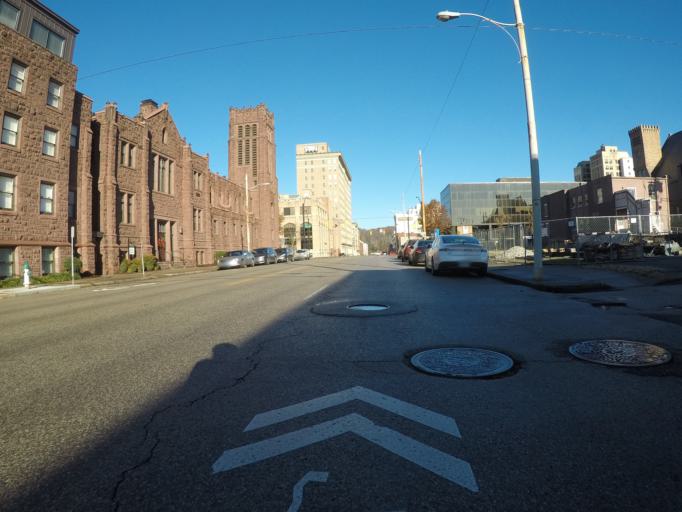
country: US
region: West Virginia
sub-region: Cabell County
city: Huntington
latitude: 38.4190
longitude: -82.4415
